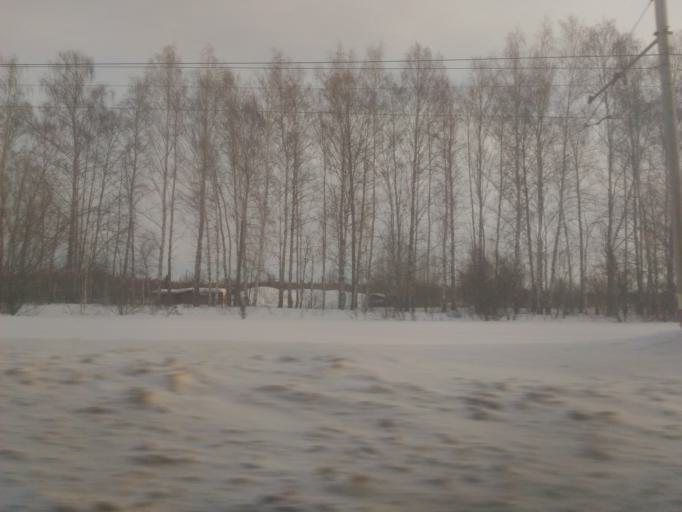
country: RU
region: Ulyanovsk
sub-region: Ulyanovskiy Rayon
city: Ulyanovsk
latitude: 54.3666
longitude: 48.3222
